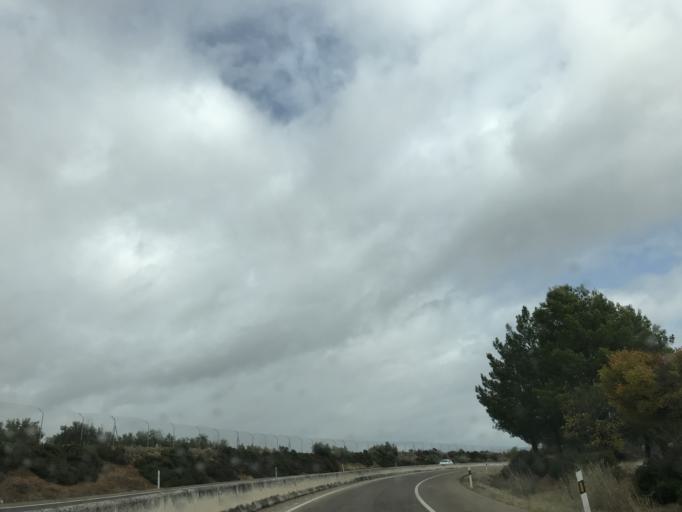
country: ES
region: Andalusia
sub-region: Provincia de Jaen
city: Bailen
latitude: 38.1238
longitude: -3.7614
